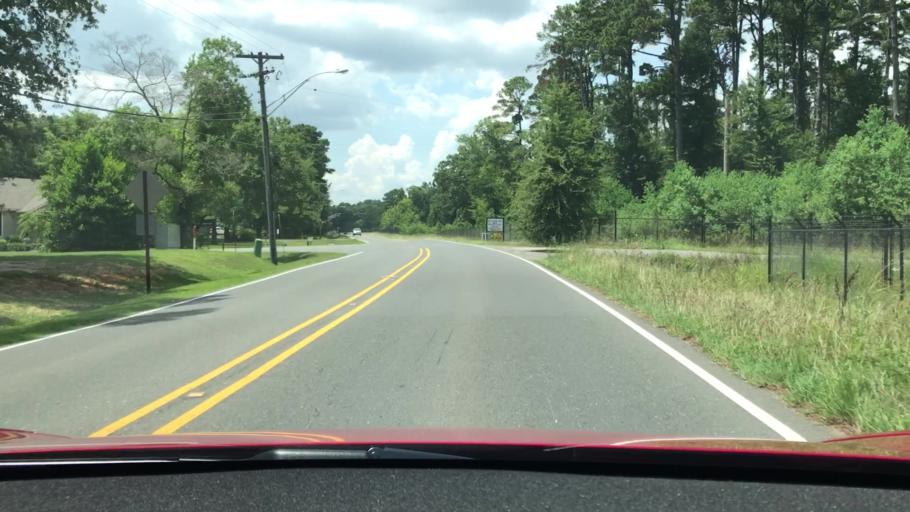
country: US
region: Louisiana
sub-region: Bossier Parish
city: Bossier City
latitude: 32.3864
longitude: -93.7175
